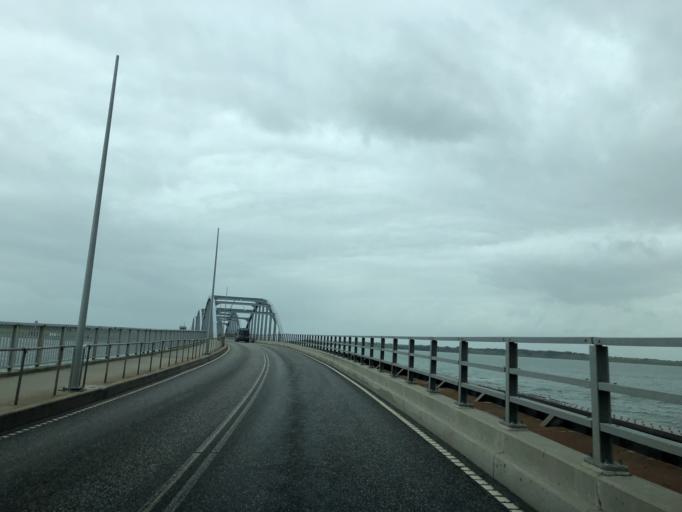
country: DK
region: Central Jutland
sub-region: Struer Kommune
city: Struer
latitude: 56.5770
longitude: 8.5619
